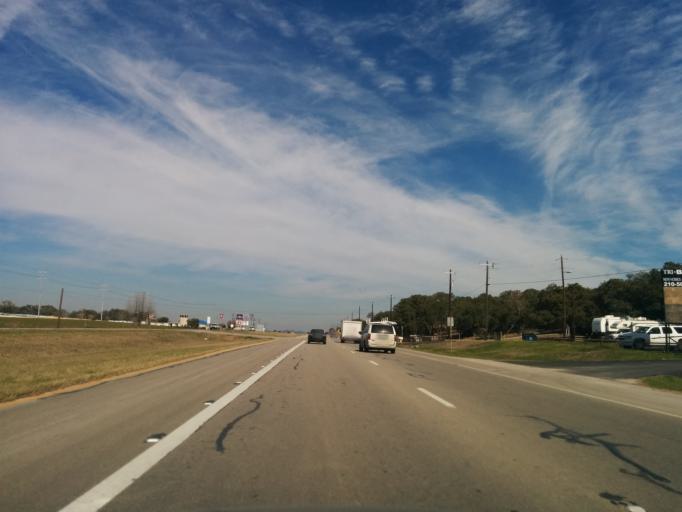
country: US
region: Texas
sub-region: Comal County
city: Bulverde
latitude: 29.8063
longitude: -98.4174
